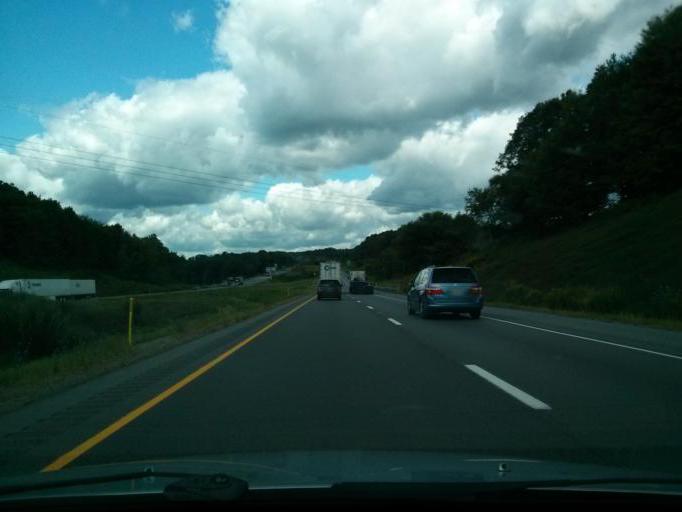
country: US
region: Pennsylvania
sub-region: Clearfield County
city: DuBois
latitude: 41.1404
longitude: -78.7412
